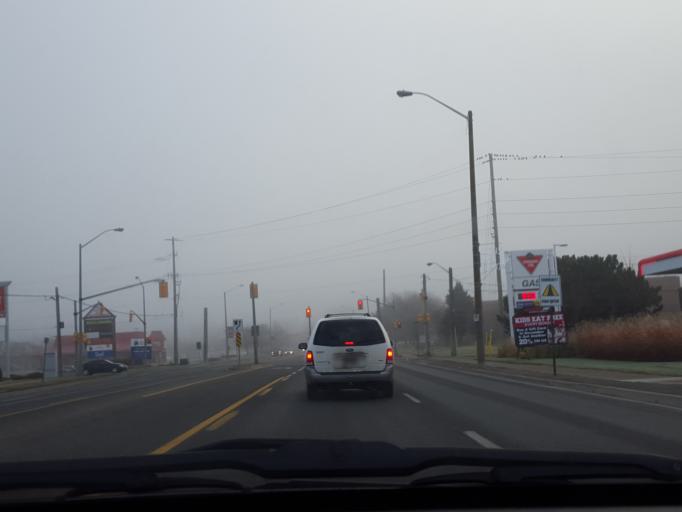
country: CA
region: Ontario
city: Angus
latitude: 44.1480
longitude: -79.8834
